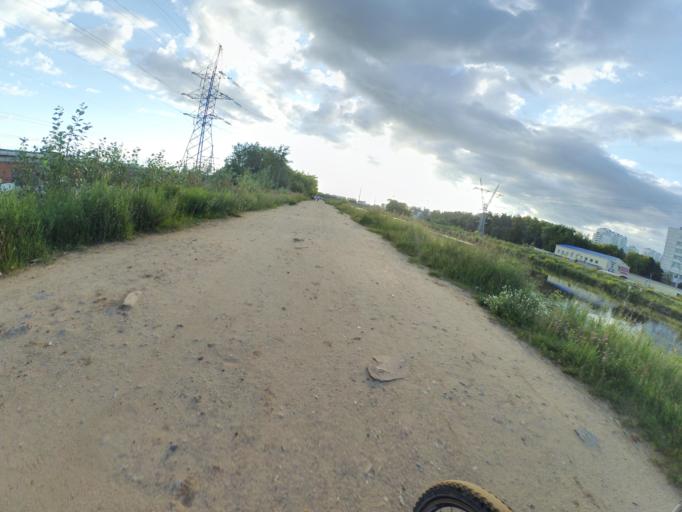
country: RU
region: Moscow
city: Pokrovskoye-Streshnevo
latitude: 55.8358
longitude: 37.4434
